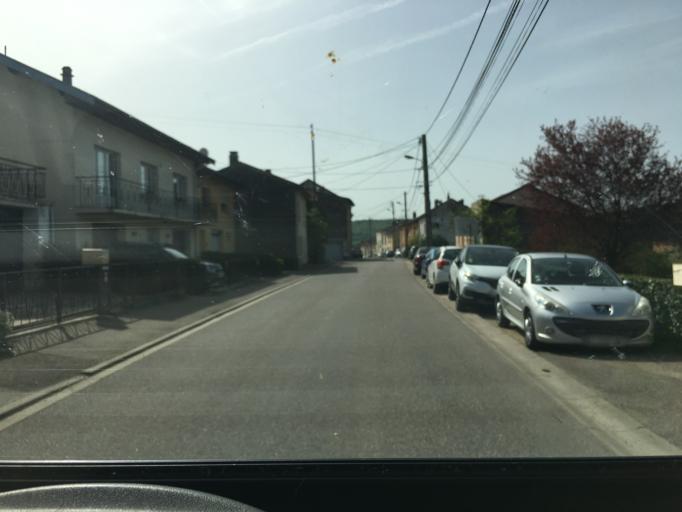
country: FR
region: Lorraine
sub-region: Departement de Meurthe-et-Moselle
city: Chaligny
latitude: 48.6376
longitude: 6.0451
